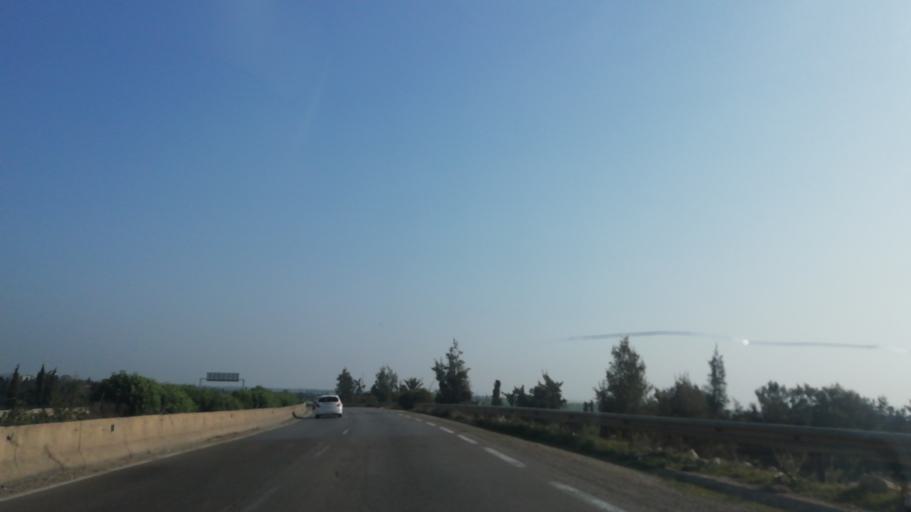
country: DZ
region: Oran
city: Bou Tlelis
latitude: 35.5660
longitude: -0.9044
